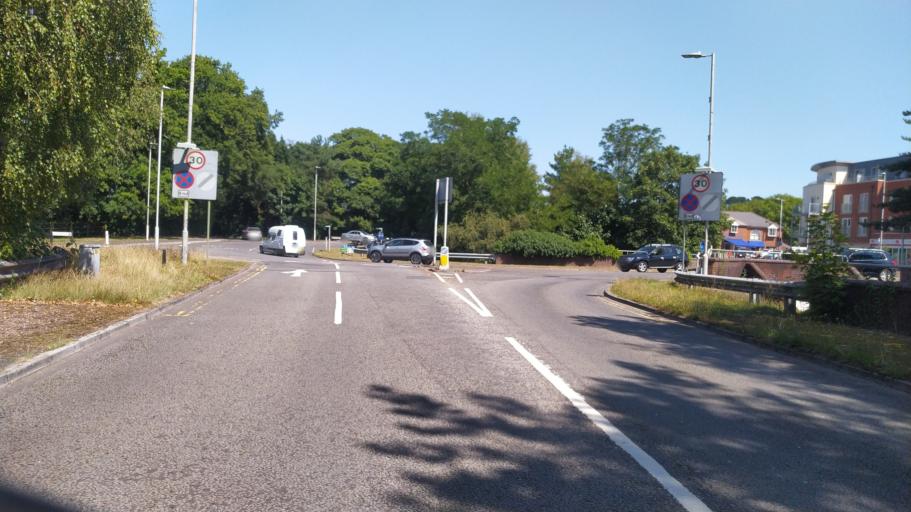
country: GB
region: England
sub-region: Dorset
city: Broadstone
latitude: 50.7614
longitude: -1.9966
